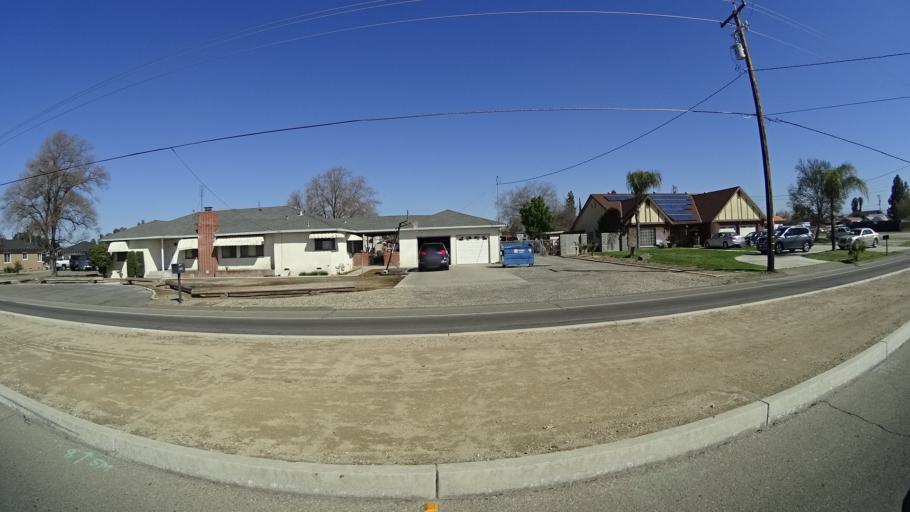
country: US
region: California
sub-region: Fresno County
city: West Park
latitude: 36.7645
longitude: -119.8767
